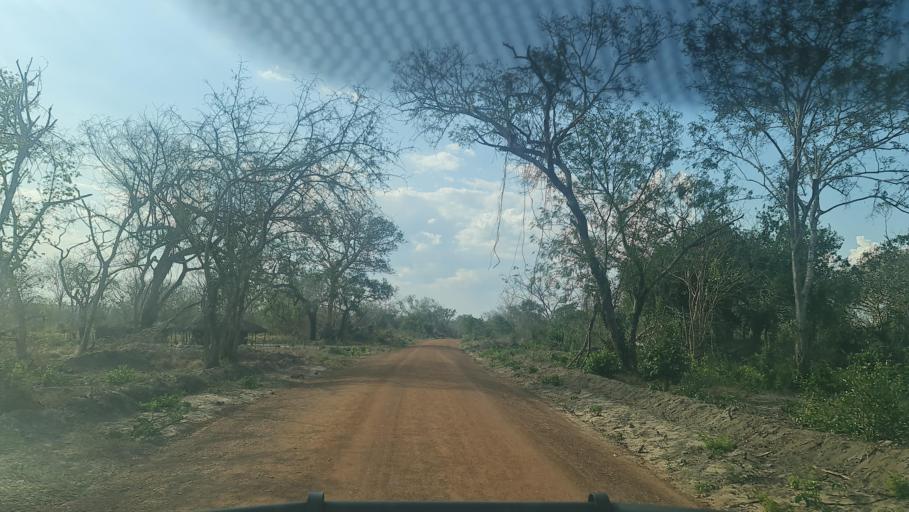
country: MZ
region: Nampula
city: Ilha de Mocambique
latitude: -15.5045
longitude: 40.1630
